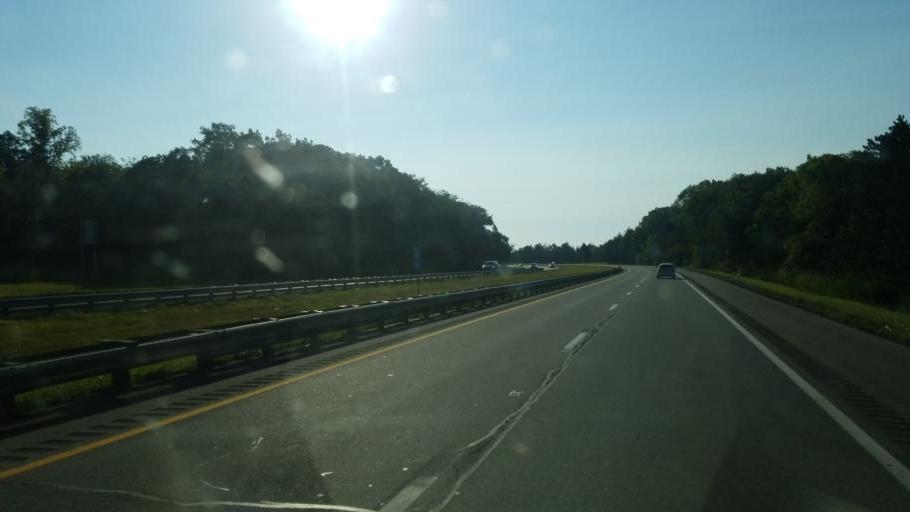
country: US
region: Ohio
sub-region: Cuyahoga County
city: Solon
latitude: 41.3965
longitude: -81.4505
